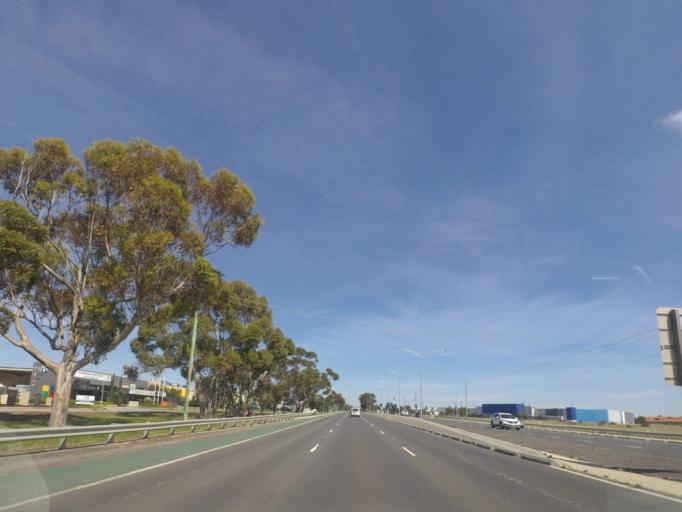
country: AU
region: Victoria
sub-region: Melton
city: Caroline Springs
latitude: -37.7615
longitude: 144.7525
